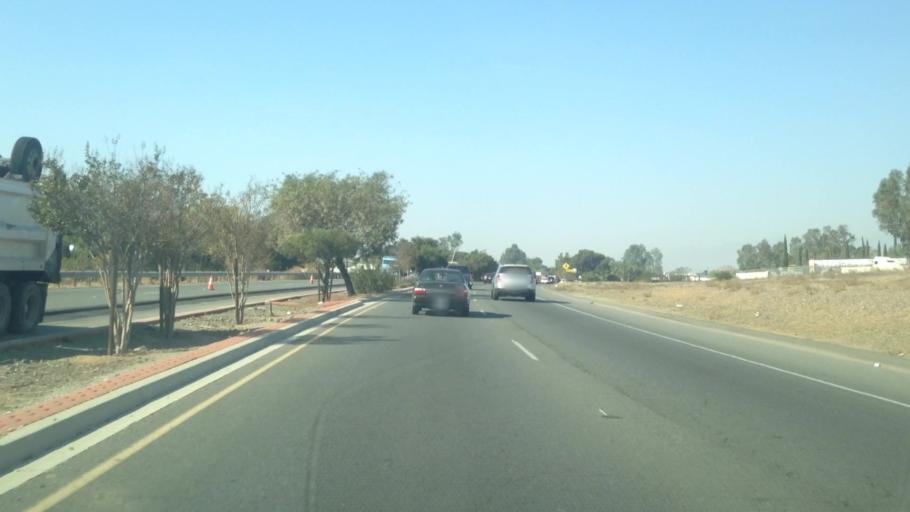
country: US
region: California
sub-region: Riverside County
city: Pedley
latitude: 33.9696
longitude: -117.4708
